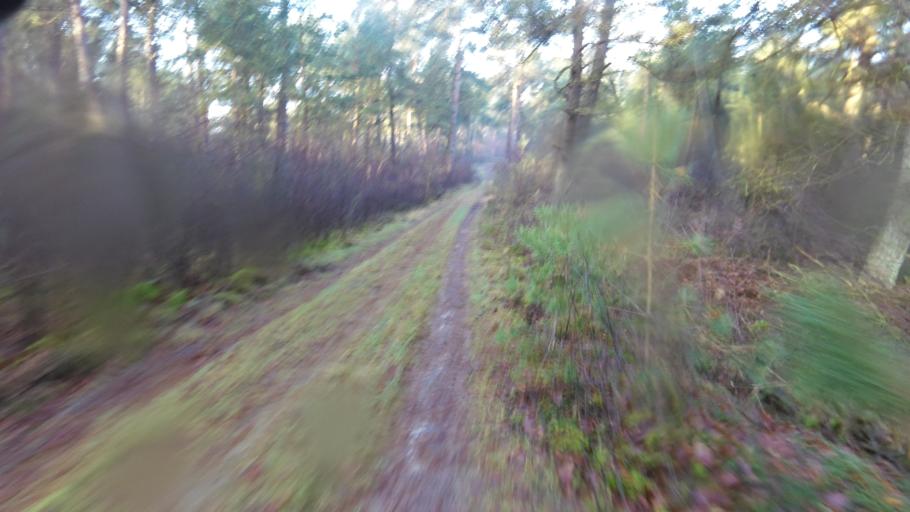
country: NL
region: Gelderland
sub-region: Gemeente Barneveld
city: Garderen
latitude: 52.2036
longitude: 5.7383
